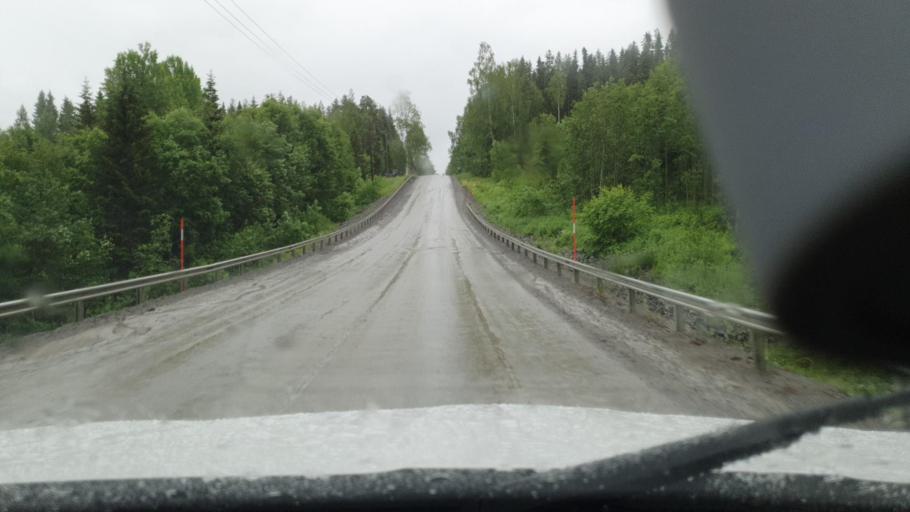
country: SE
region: Vaesterbotten
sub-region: Skelleftea Kommun
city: Burtraesk
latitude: 64.3544
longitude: 20.4781
